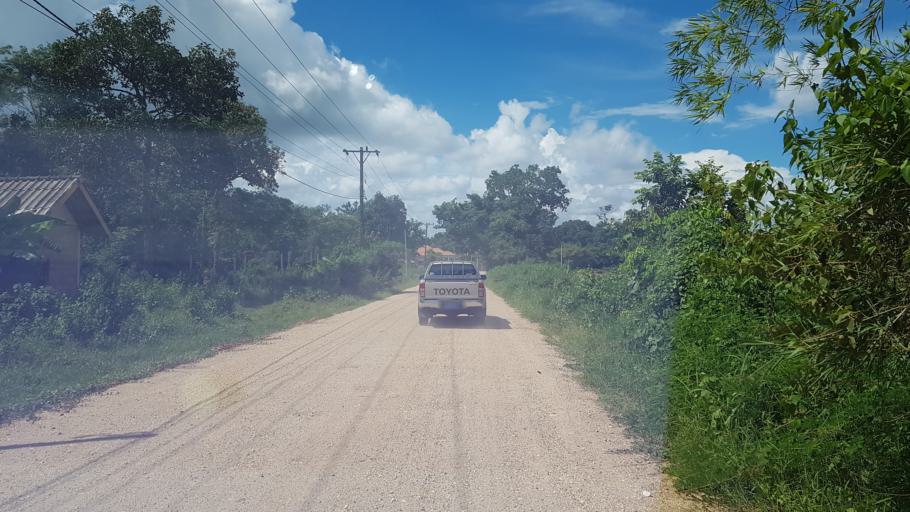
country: LA
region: Vientiane
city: Vientiane
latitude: 18.2224
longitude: 102.5178
